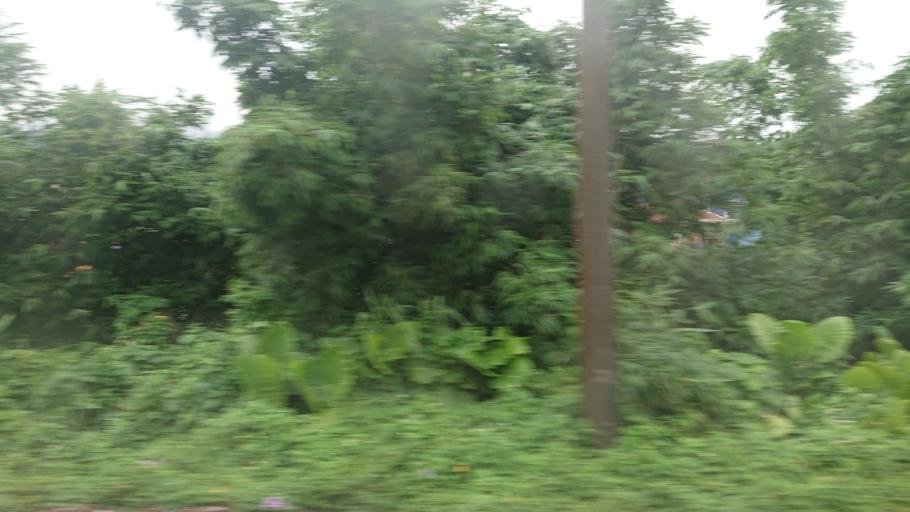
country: TW
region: Taiwan
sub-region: Keelung
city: Keelung
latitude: 25.0802
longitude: 121.6847
